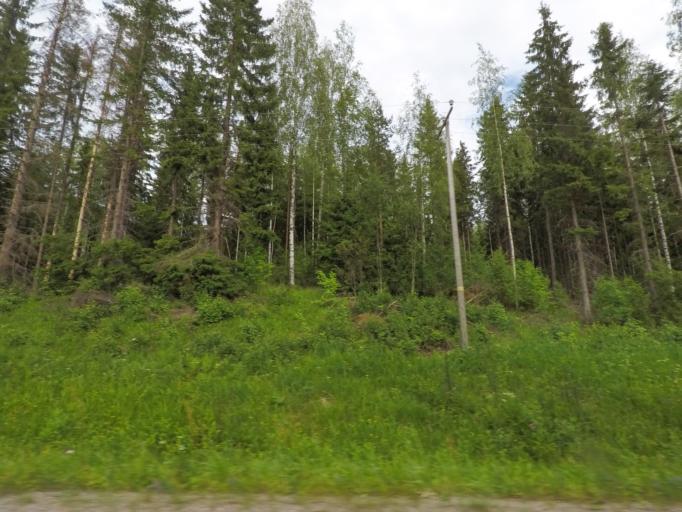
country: FI
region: Paijanne Tavastia
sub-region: Lahti
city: Hollola
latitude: 60.8751
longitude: 25.5041
